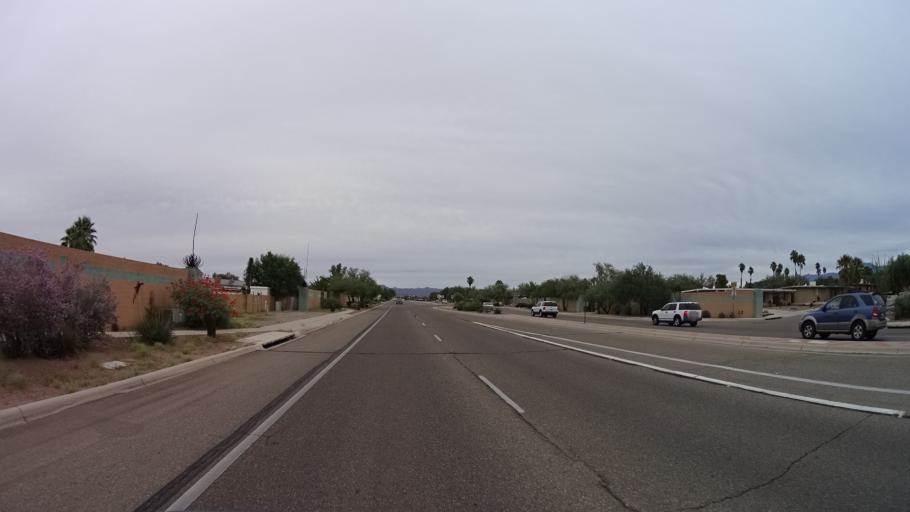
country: US
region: Arizona
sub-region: Pima County
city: Casas Adobes
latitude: 32.3479
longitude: -111.0470
